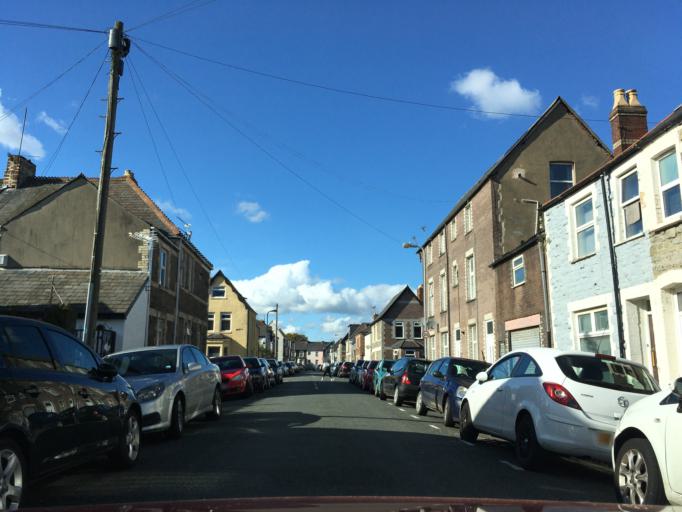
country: GB
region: Wales
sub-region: Cardiff
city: Cardiff
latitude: 51.4917
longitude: -3.1758
